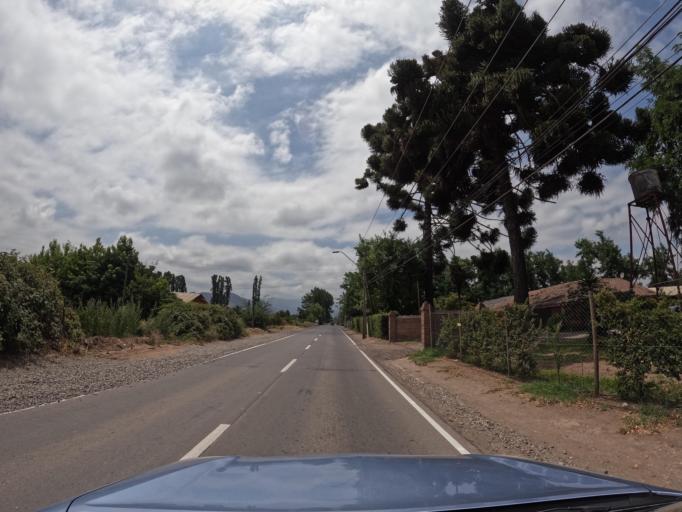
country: CL
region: O'Higgins
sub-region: Provincia de Colchagua
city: Chimbarongo
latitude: -34.7304
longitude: -70.9917
